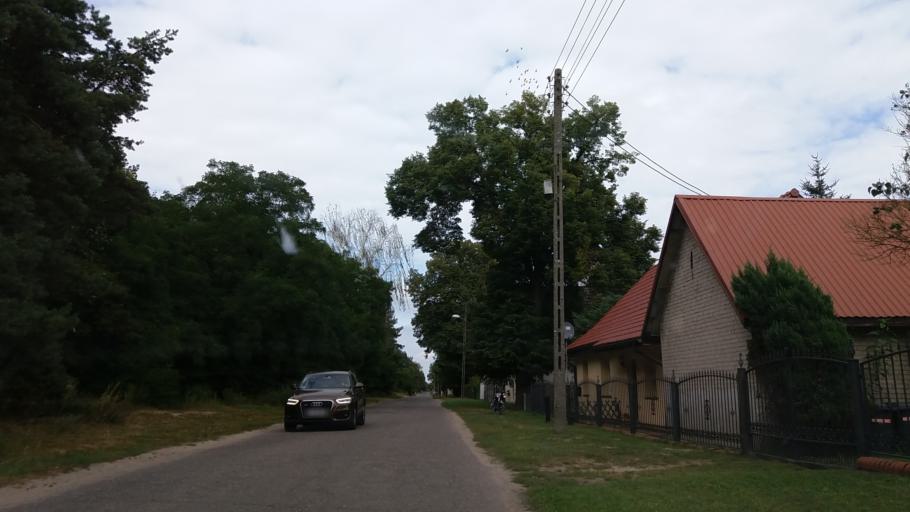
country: PL
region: West Pomeranian Voivodeship
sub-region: Powiat stargardzki
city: Kobylanka
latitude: 53.3334
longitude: 14.8906
